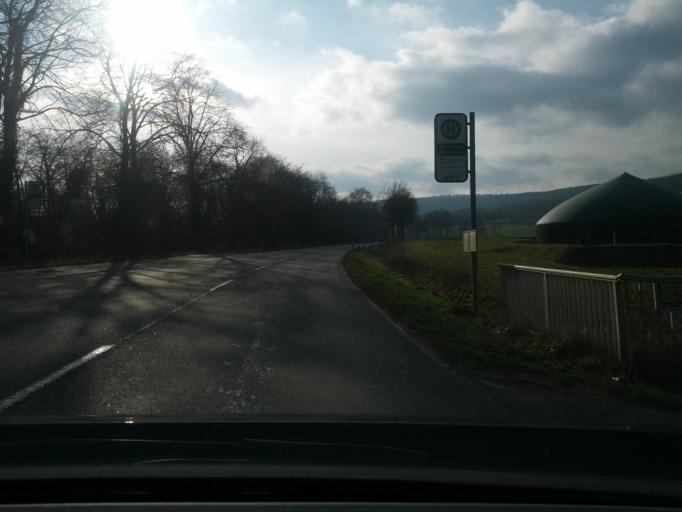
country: DE
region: Lower Saxony
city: Hannoversch Munden
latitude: 51.4473
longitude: 9.6388
